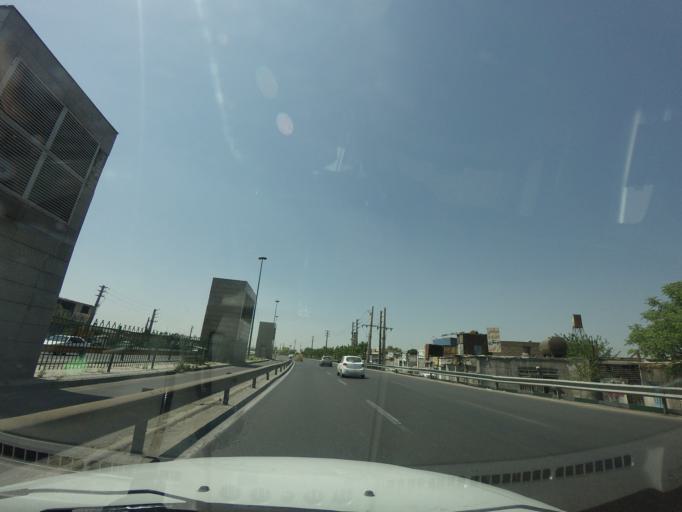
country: IR
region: Tehran
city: Tehran
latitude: 35.6277
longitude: 51.3350
